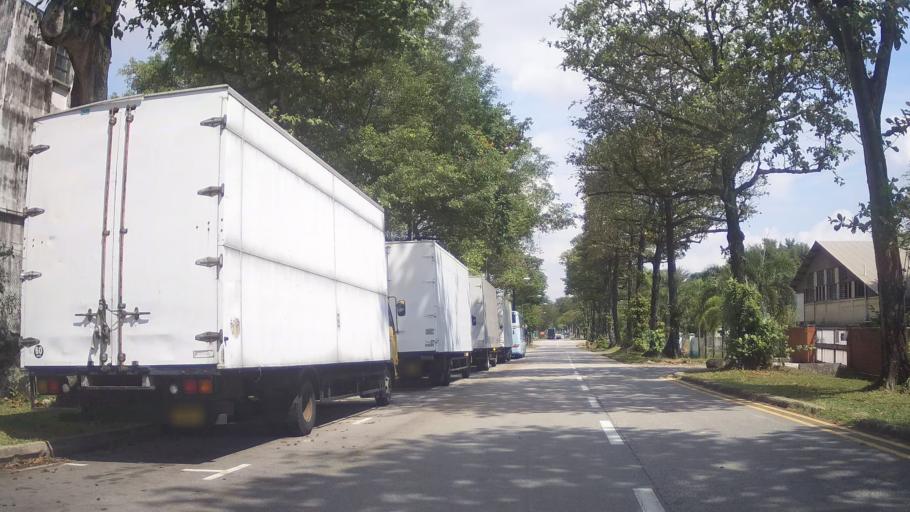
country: SG
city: Singapore
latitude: 1.3269
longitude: 103.7133
